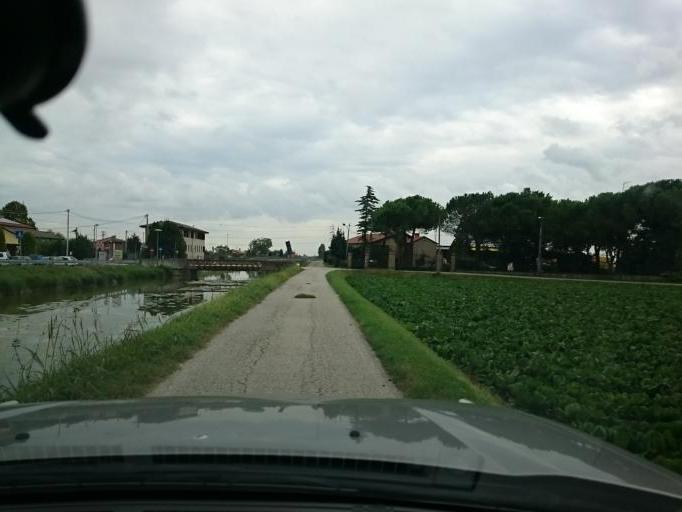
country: IT
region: Veneto
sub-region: Provincia di Padova
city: Codevigo
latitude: 45.2426
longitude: 12.1222
